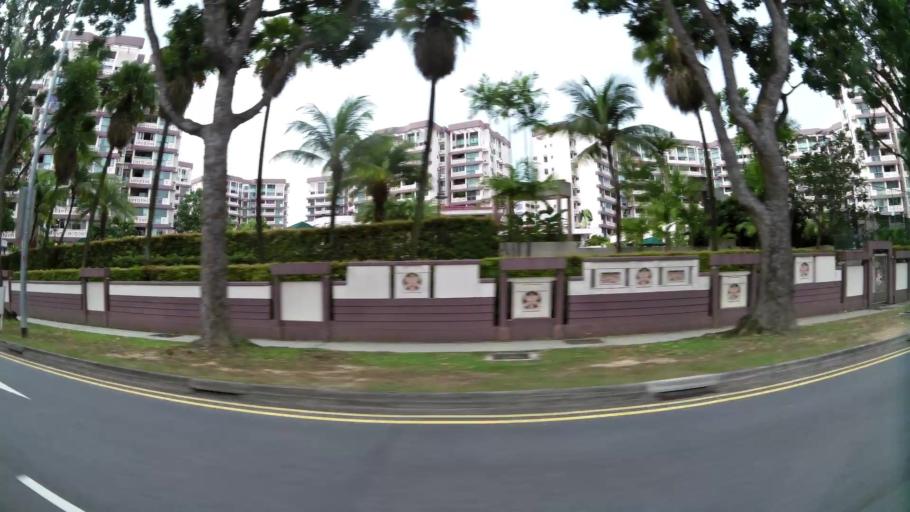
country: MY
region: Johor
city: Kampung Pasir Gudang Baru
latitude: 1.4123
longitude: 103.8360
